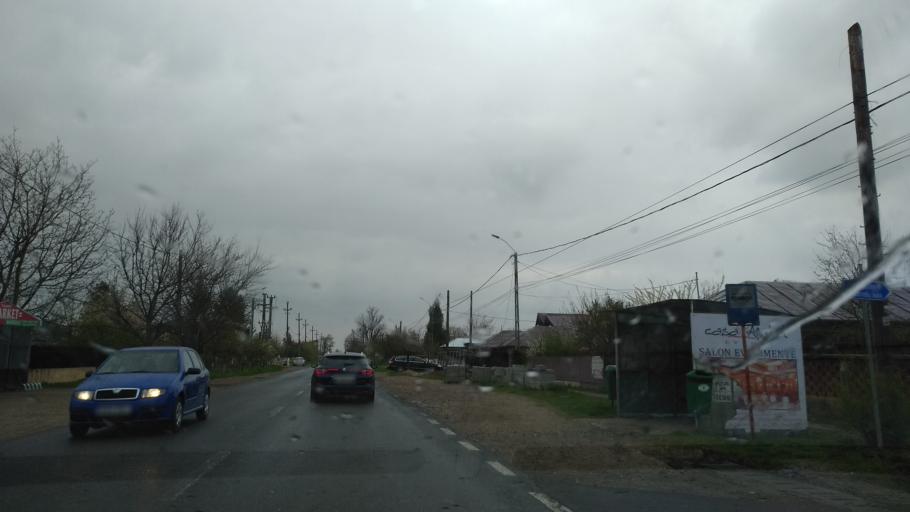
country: RO
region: Calarasi
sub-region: Comuna Frumusani
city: Frumusani
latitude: 44.2864
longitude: 26.3254
